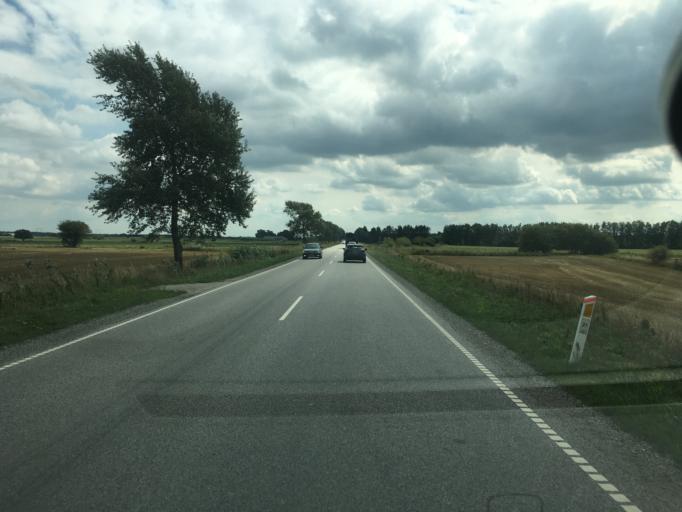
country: DK
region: South Denmark
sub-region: Aabenraa Kommune
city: Tinglev
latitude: 54.9781
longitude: 9.2983
